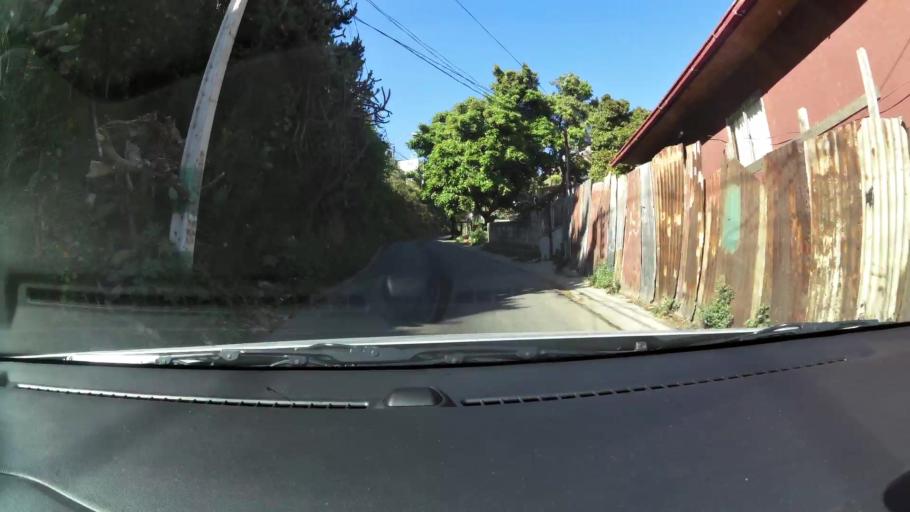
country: CL
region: Valparaiso
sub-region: Provincia de Valparaiso
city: Valparaiso
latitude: -33.0506
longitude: -71.6344
